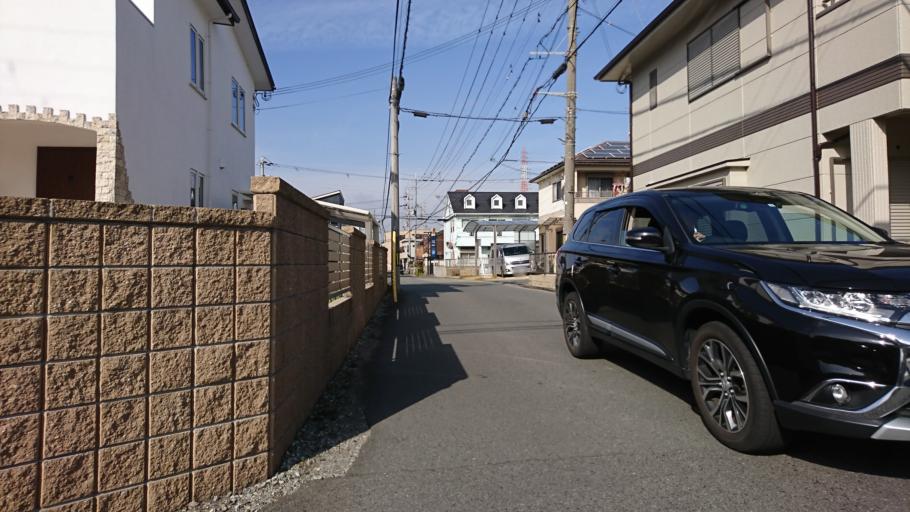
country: JP
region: Hyogo
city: Kakogawacho-honmachi
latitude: 34.7392
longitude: 134.8348
